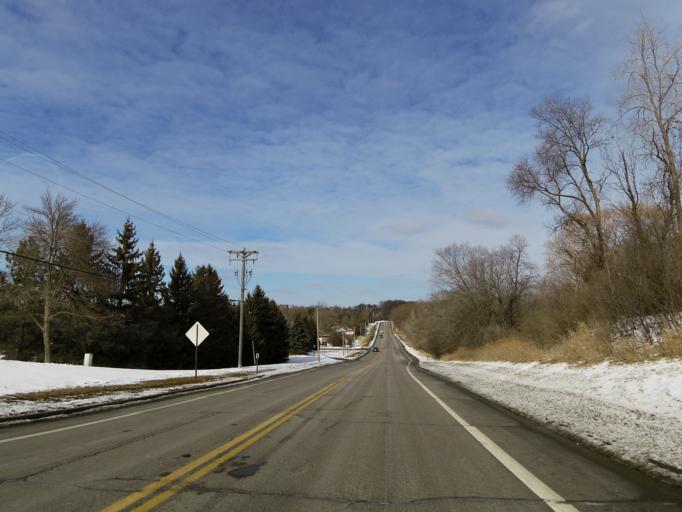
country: US
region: Minnesota
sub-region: Scott County
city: Savage
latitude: 44.8187
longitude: -93.3788
